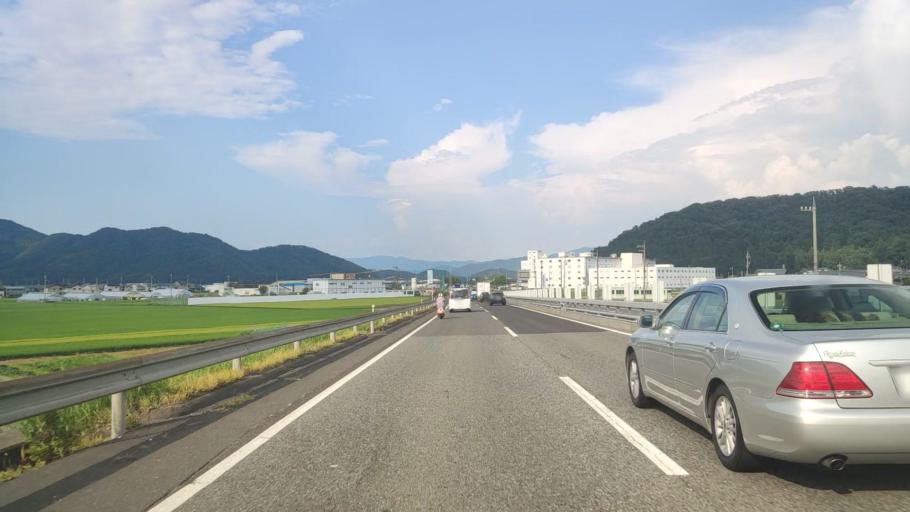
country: JP
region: Fukui
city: Takefu
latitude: 35.8788
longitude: 136.1703
